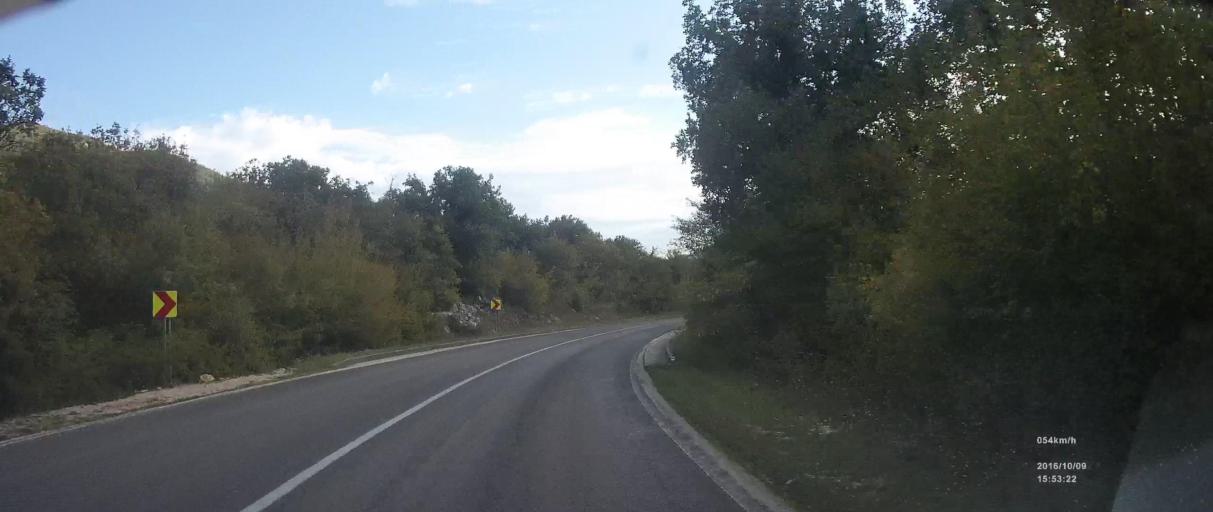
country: HR
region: Splitsko-Dalmatinska
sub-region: Grad Trogir
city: Trogir
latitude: 43.6059
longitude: 16.2251
